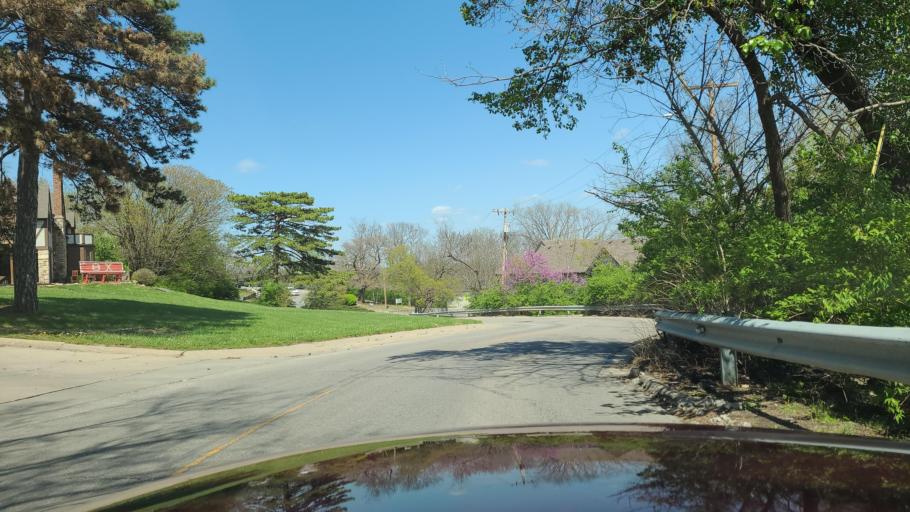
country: US
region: Kansas
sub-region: Douglas County
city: Lawrence
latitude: 38.9655
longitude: -95.2527
